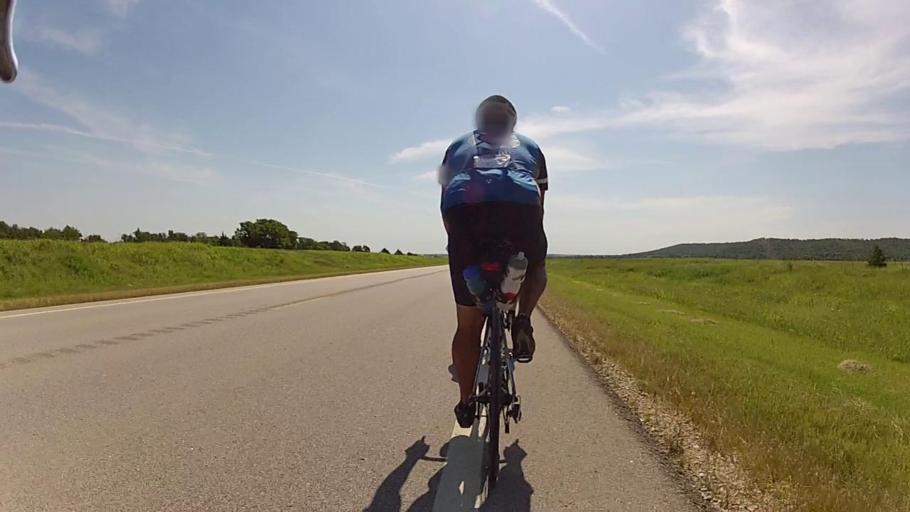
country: US
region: Kansas
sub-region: Chautauqua County
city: Sedan
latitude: 37.1067
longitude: -96.5651
